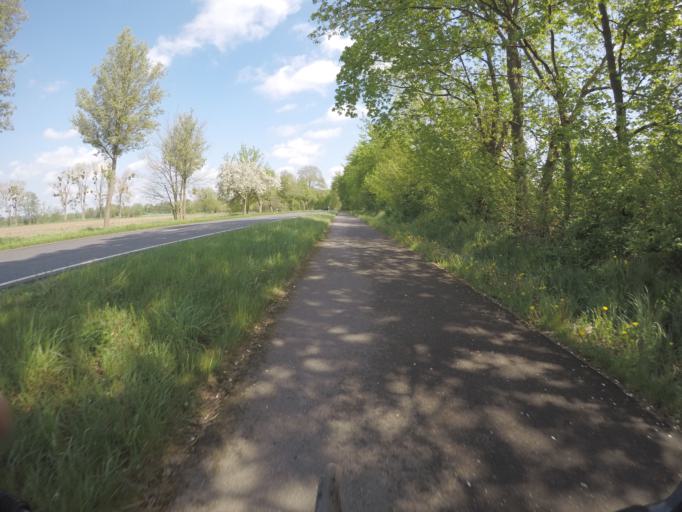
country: DE
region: Brandenburg
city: Marienwerder
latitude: 52.8336
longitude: 13.5697
